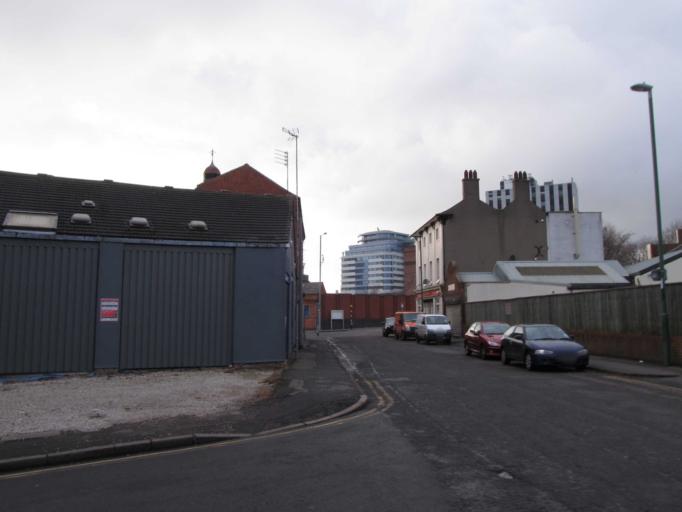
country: GB
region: England
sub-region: Nottingham
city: Nottingham
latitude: 52.9553
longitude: -1.1370
